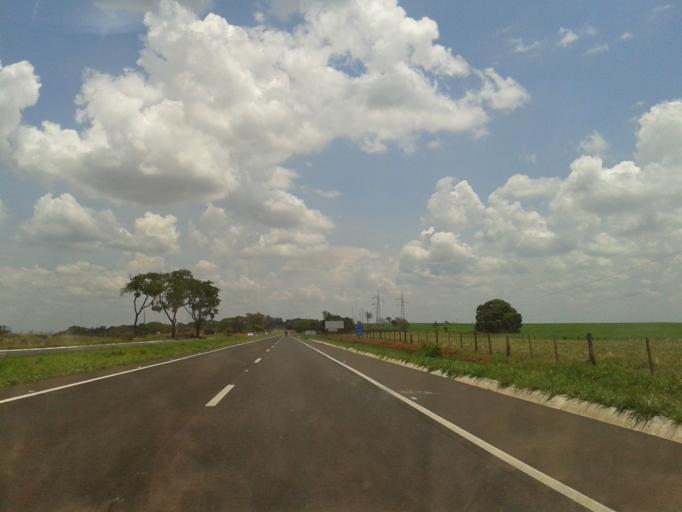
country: BR
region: Minas Gerais
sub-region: Monte Alegre De Minas
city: Monte Alegre de Minas
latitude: -18.8498
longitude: -48.8313
